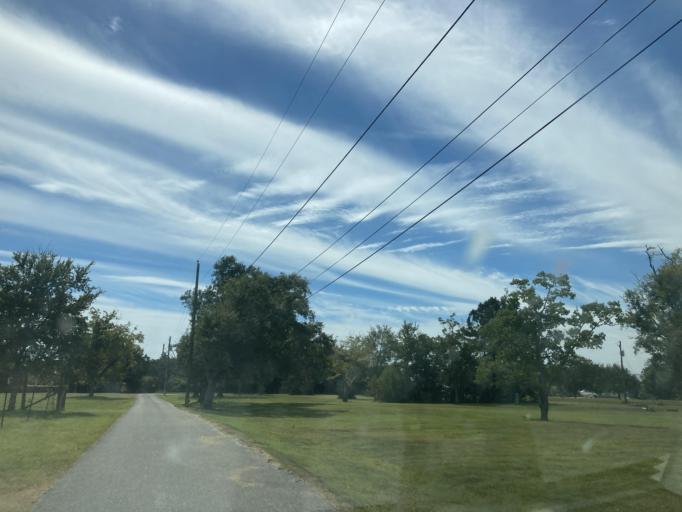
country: US
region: Mississippi
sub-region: Harrison County
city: D'Iberville
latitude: 30.4270
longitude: -88.8771
